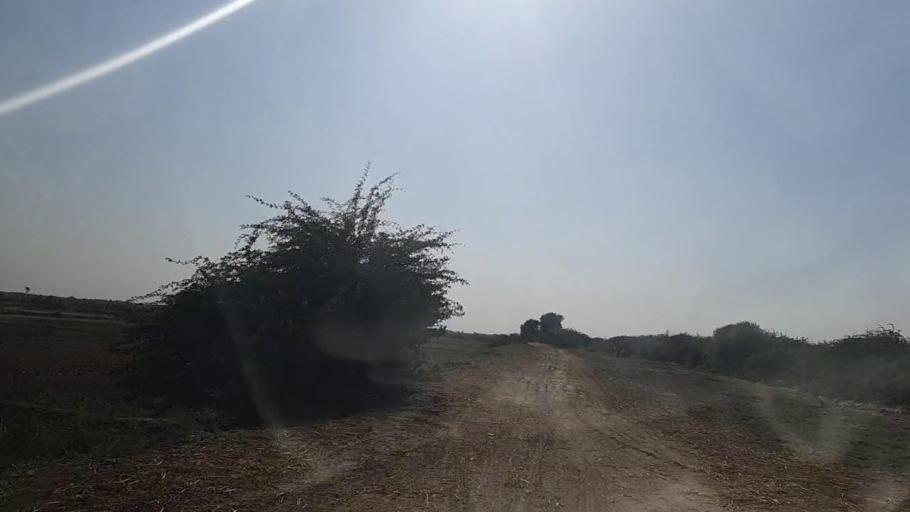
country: PK
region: Sindh
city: Mirpur Batoro
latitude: 24.6490
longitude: 68.1758
